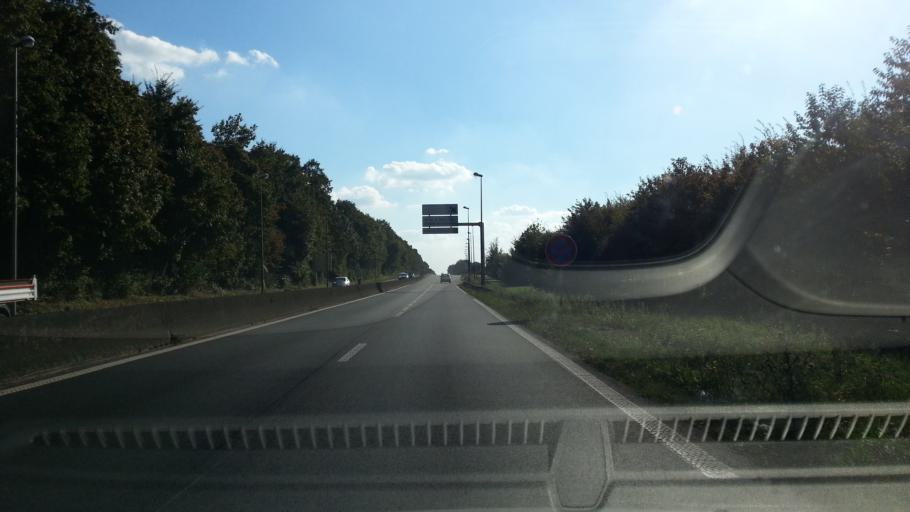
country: FR
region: Picardie
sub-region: Departement de l'Oise
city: Creil
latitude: 49.2435
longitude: 2.4744
